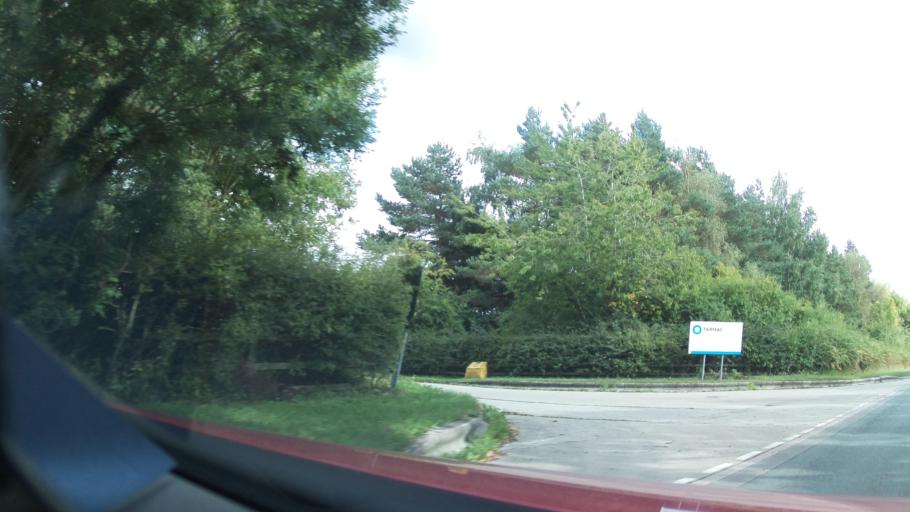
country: GB
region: England
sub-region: North Yorkshire
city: Bedale
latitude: 54.2367
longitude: -1.6759
